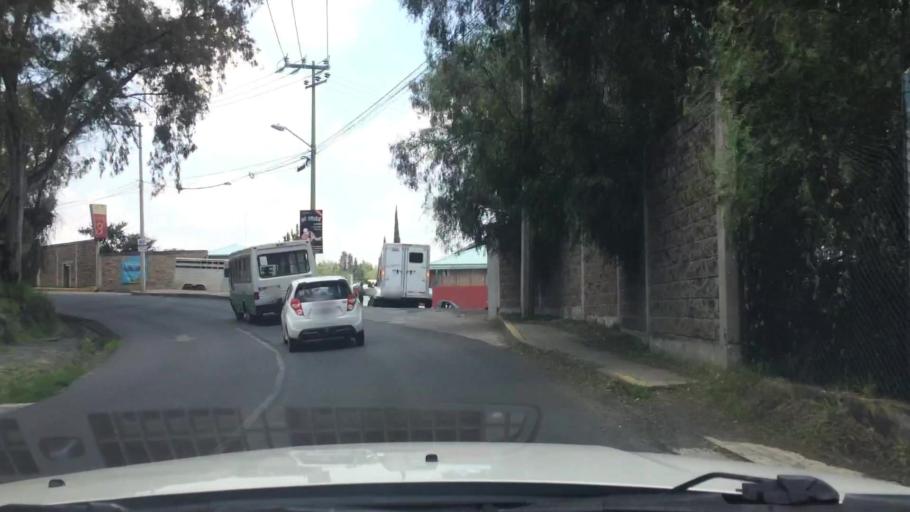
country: MX
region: Mexico City
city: Miguel Hidalgo
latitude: 19.4364
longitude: -99.2271
